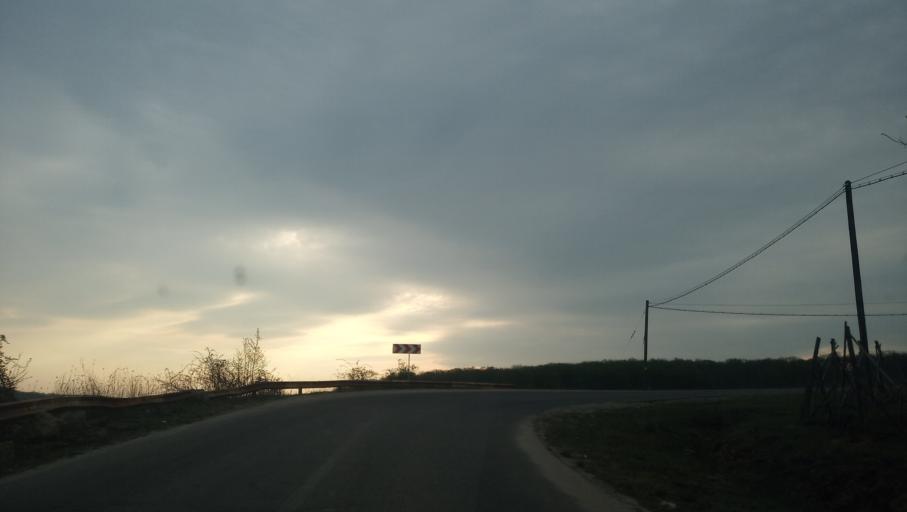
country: RO
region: Bihor
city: Hidiselu de Sus
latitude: 46.9259
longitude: 22.0538
